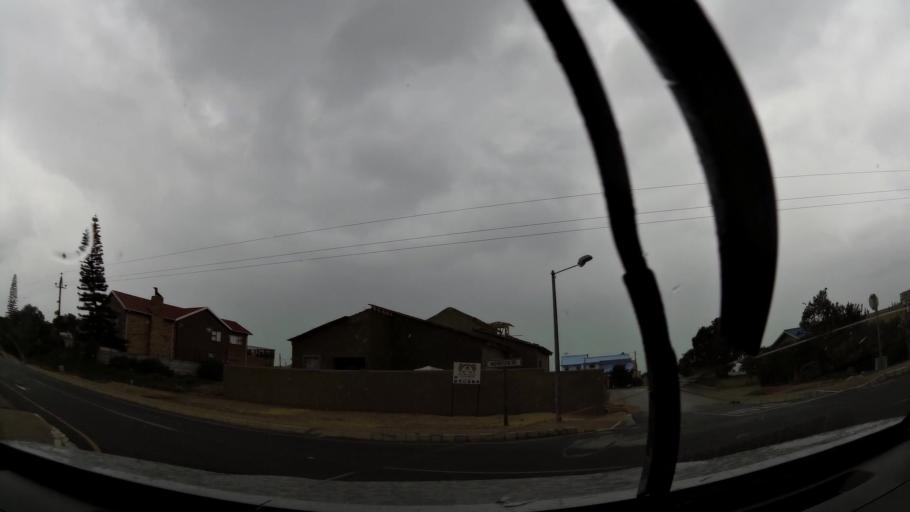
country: ZA
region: Western Cape
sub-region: Eden District Municipality
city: George
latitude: -34.0491
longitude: 22.2896
